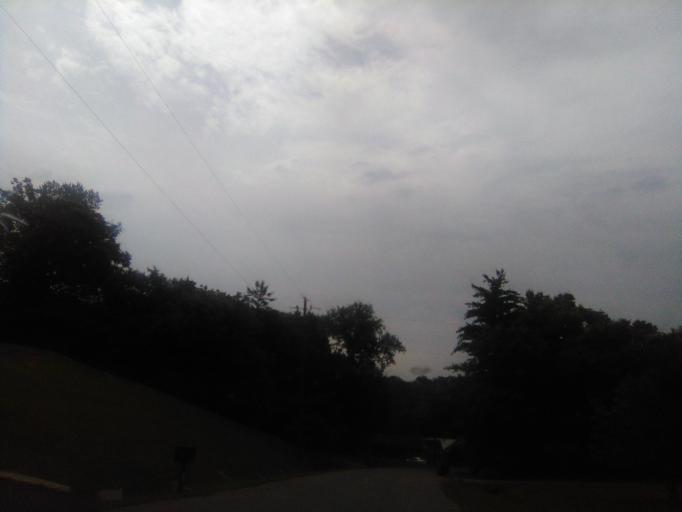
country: US
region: Tennessee
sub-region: Davidson County
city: Belle Meade
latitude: 36.0928
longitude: -86.8984
